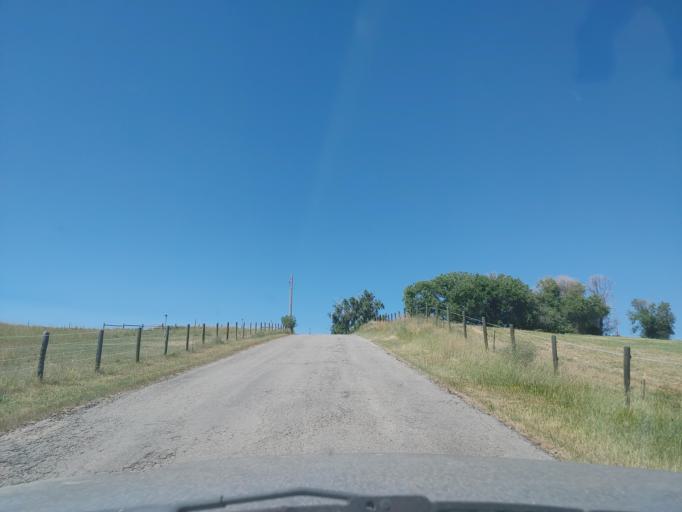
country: US
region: Montana
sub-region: Ravalli County
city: Hamilton
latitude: 46.3147
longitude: -114.0612
